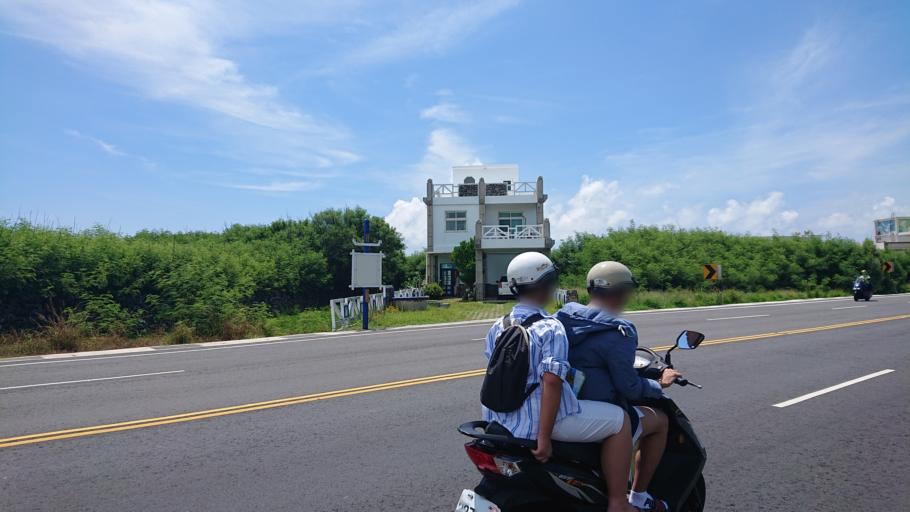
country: TW
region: Taiwan
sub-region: Penghu
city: Ma-kung
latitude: 23.6132
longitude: 119.6083
